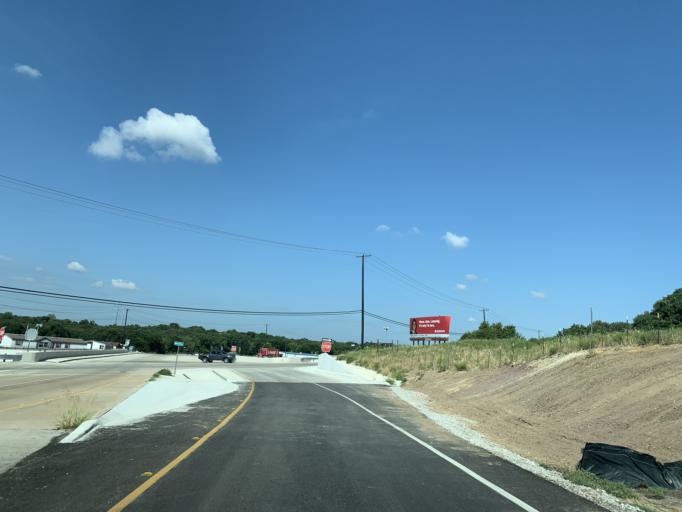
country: US
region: Texas
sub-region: Tarrant County
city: Lakeside
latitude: 32.8595
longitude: -97.5168
